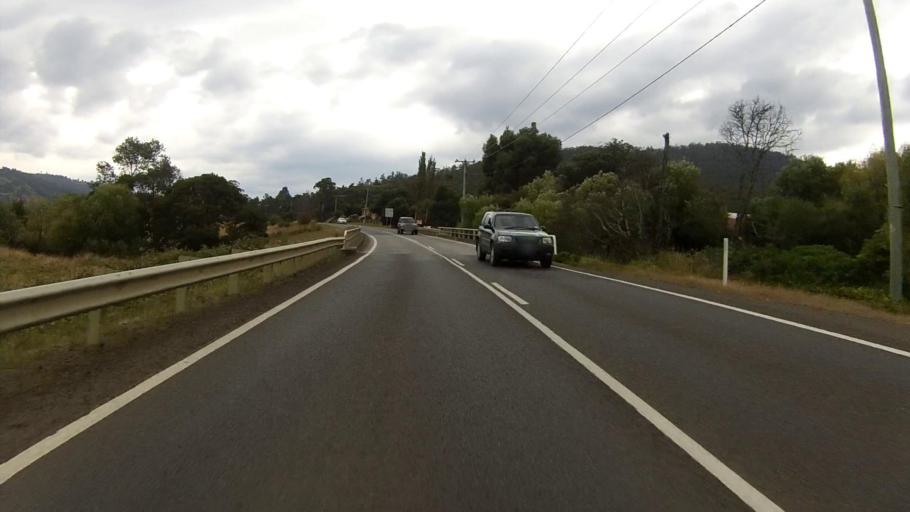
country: AU
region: Tasmania
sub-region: Huon Valley
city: Franklin
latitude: -43.0702
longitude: 147.0406
